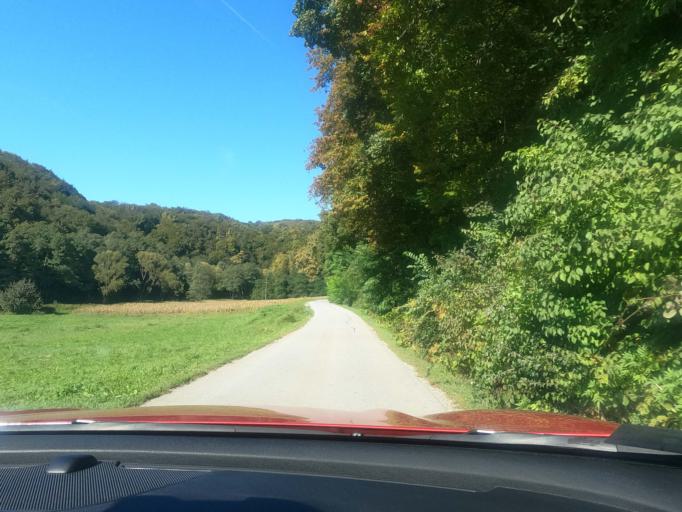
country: HR
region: Sisacko-Moslavacka
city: Petrinja
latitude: 45.3888
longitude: 16.2467
